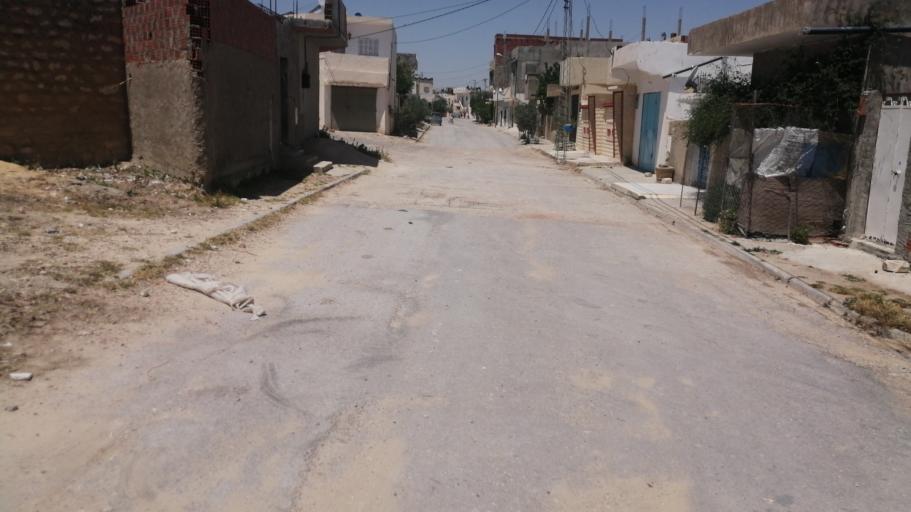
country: TN
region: Silyanah
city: Maktar
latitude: 35.8579
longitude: 9.2121
